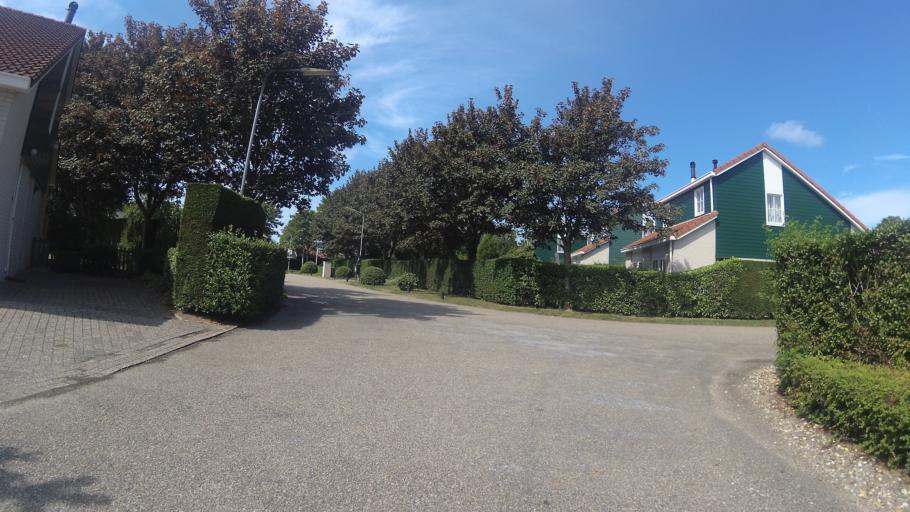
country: NL
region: Zeeland
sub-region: Schouwen-Duiveland
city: Burgh
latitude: 51.6861
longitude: 3.7302
